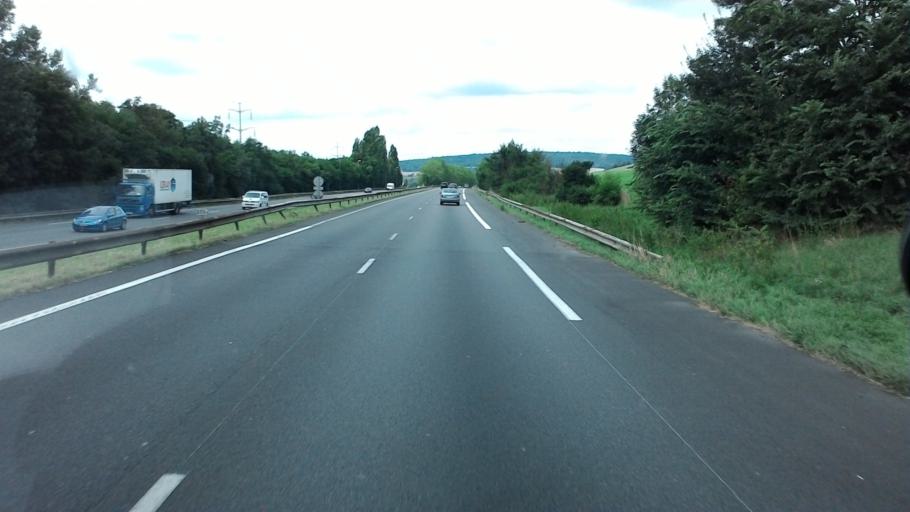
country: FR
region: Lorraine
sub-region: Departement de Meurthe-et-Moselle
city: Frouard
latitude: 48.7695
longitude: 6.1438
